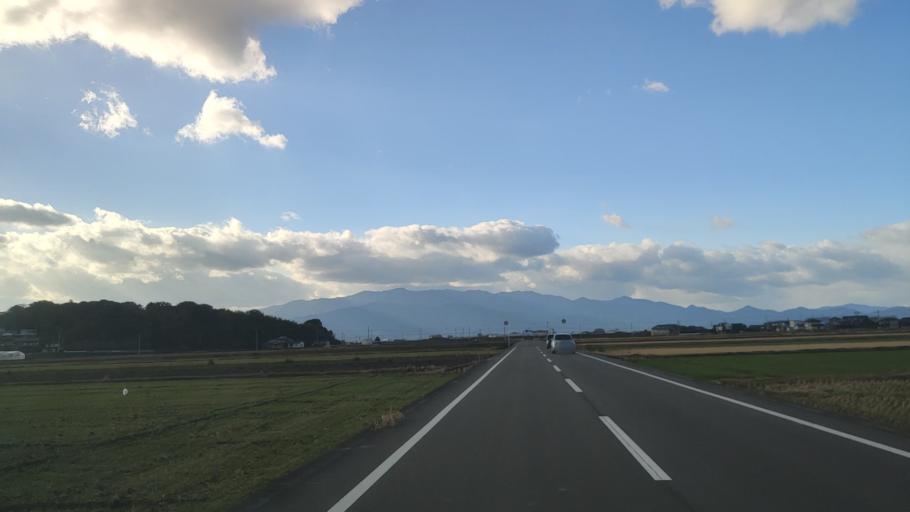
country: JP
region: Ehime
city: Saijo
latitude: 33.9035
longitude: 133.1348
